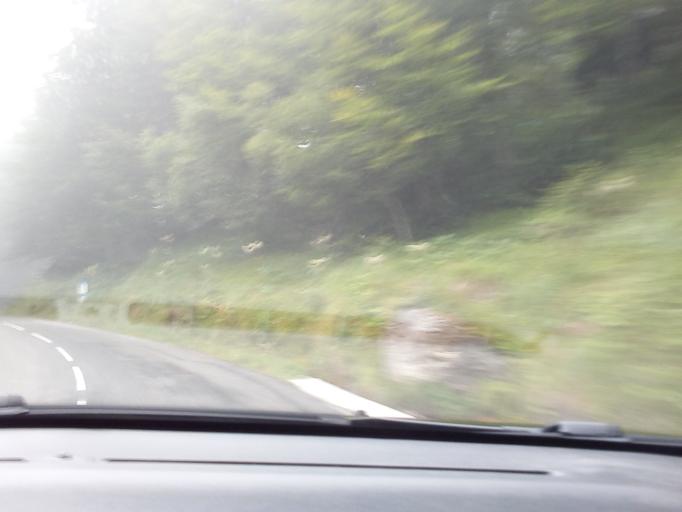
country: FR
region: Aquitaine
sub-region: Departement des Pyrenees-Atlantiques
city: Laruns
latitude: 42.9663
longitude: -0.3344
